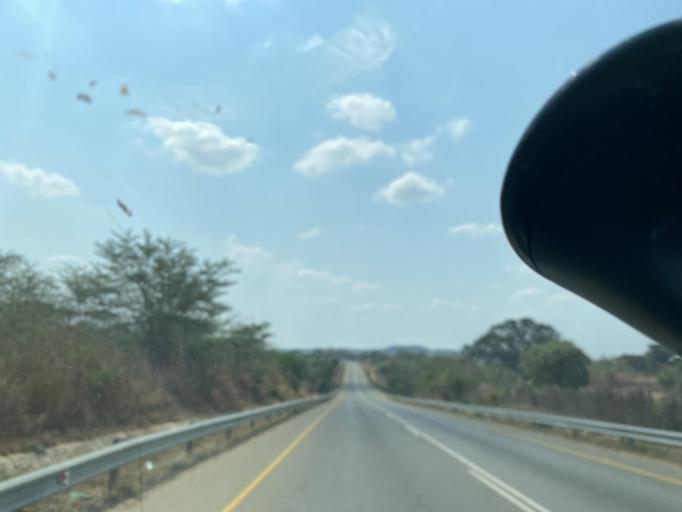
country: ZM
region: Lusaka
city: Chongwe
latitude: -15.5565
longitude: 28.6826
